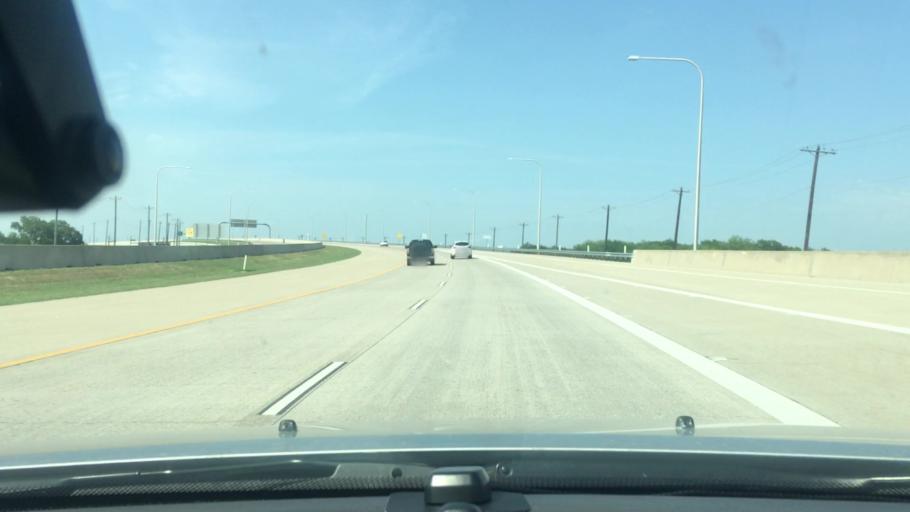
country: US
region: Texas
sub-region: Collin County
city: Prosper
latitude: 33.2039
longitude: -96.8226
